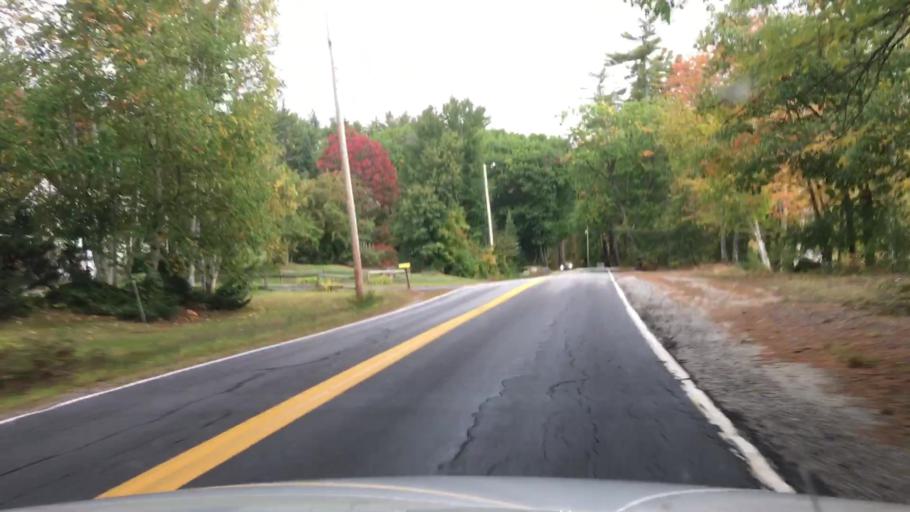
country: US
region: Maine
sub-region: Oxford County
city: Bethel
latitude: 44.3512
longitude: -70.7907
